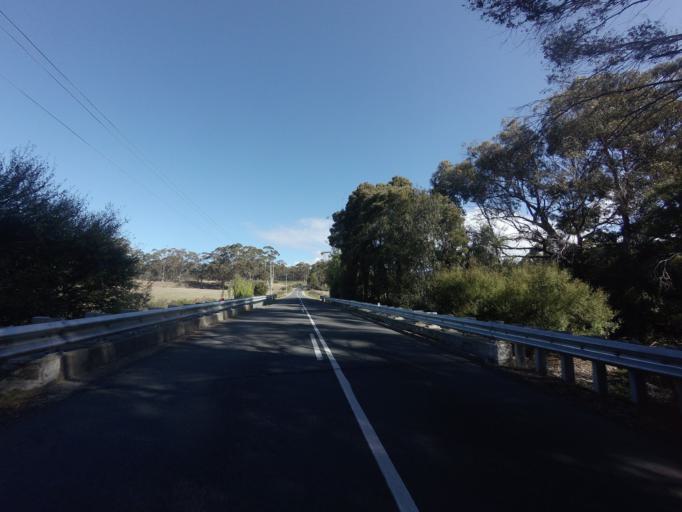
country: AU
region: Tasmania
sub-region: Break O'Day
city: St Helens
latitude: -41.6846
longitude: 148.2820
